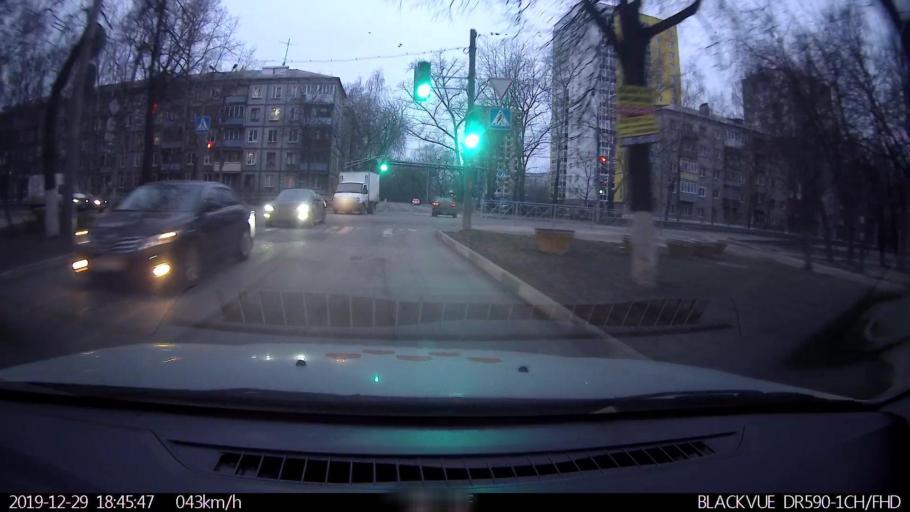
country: RU
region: Nizjnij Novgorod
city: Gorbatovka
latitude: 56.3391
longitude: 43.8454
